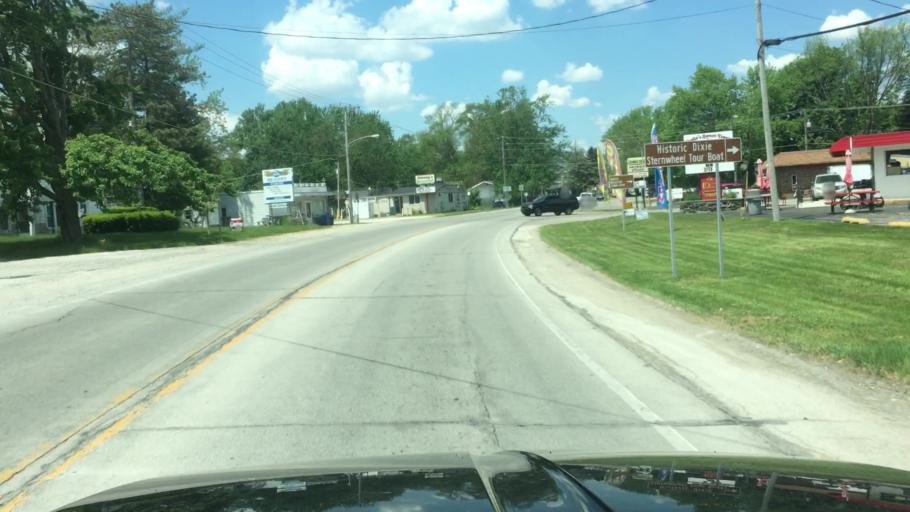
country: US
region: Indiana
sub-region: Kosciusko County
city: North Webster
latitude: 41.3218
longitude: -85.6973
